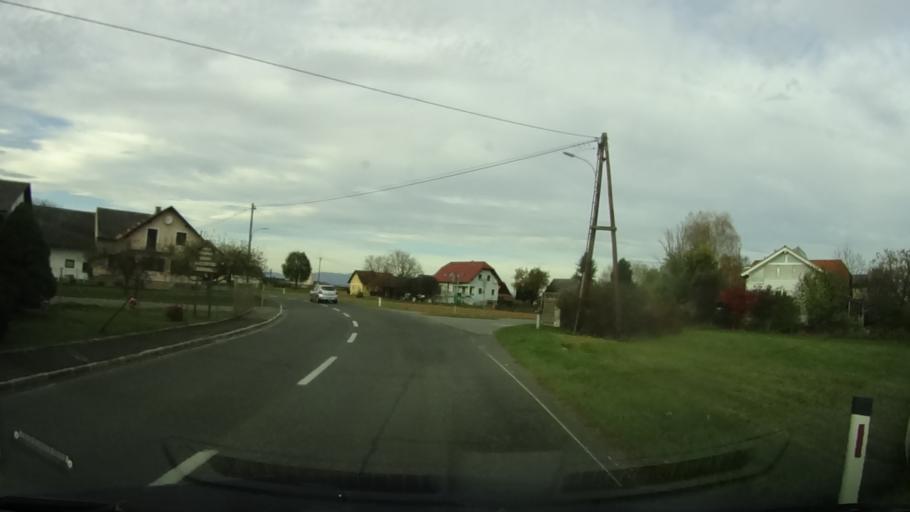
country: AT
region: Styria
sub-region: Politischer Bezirk Graz-Umgebung
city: Wundschuh
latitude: 46.9445
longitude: 15.4458
